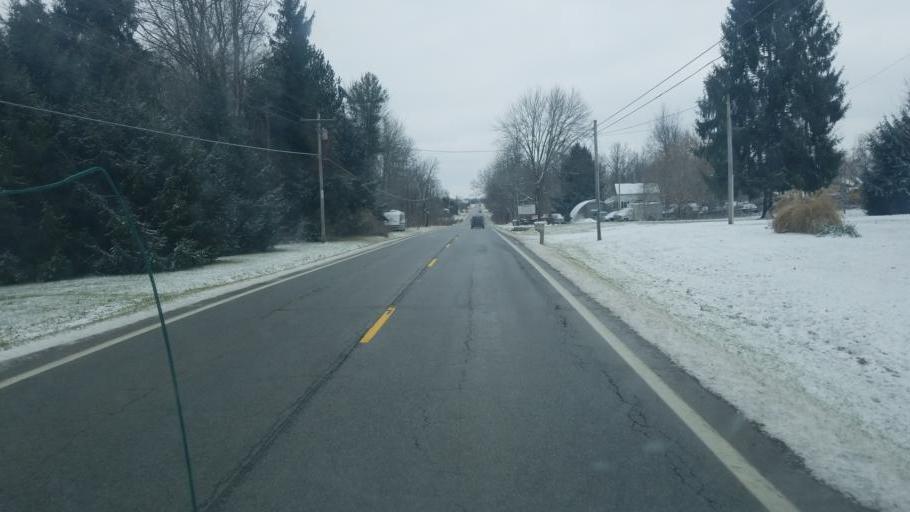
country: US
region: Ohio
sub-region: Licking County
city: Johnstown
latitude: 40.1982
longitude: -82.7686
